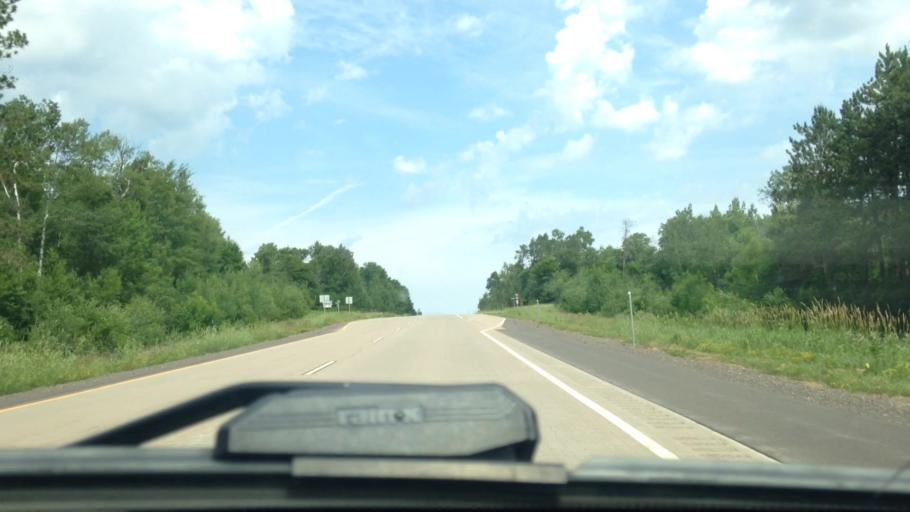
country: US
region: Wisconsin
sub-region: Douglas County
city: Lake Nebagamon
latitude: 46.2722
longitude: -91.8046
